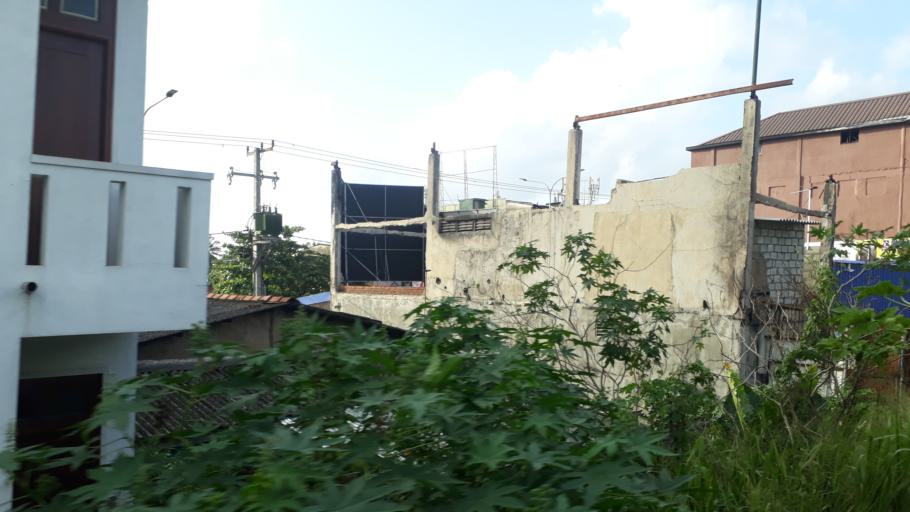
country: LK
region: Western
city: Peliyagoda
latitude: 6.9583
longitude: 79.8909
